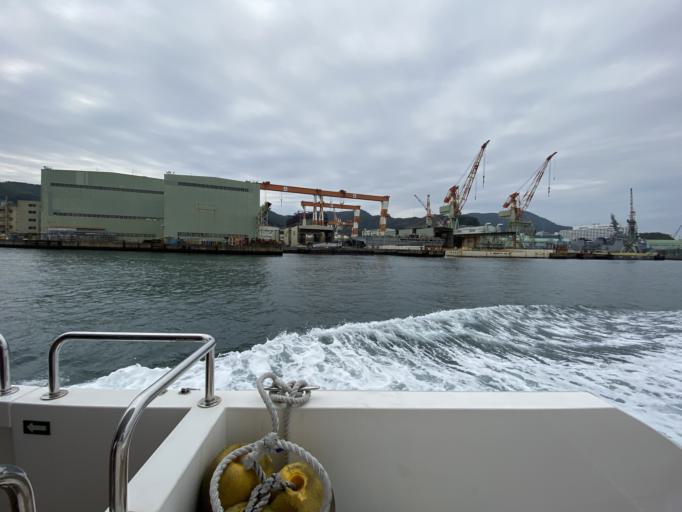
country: JP
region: Nagasaki
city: Nagasaki-shi
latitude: 32.7311
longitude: 129.8576
